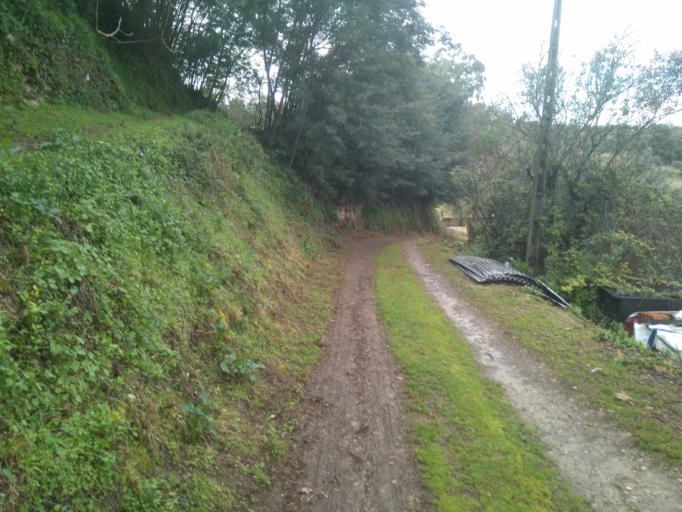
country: PT
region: Leiria
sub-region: Porto de Mos
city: Porto de Mos
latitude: 39.6040
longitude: -8.8176
